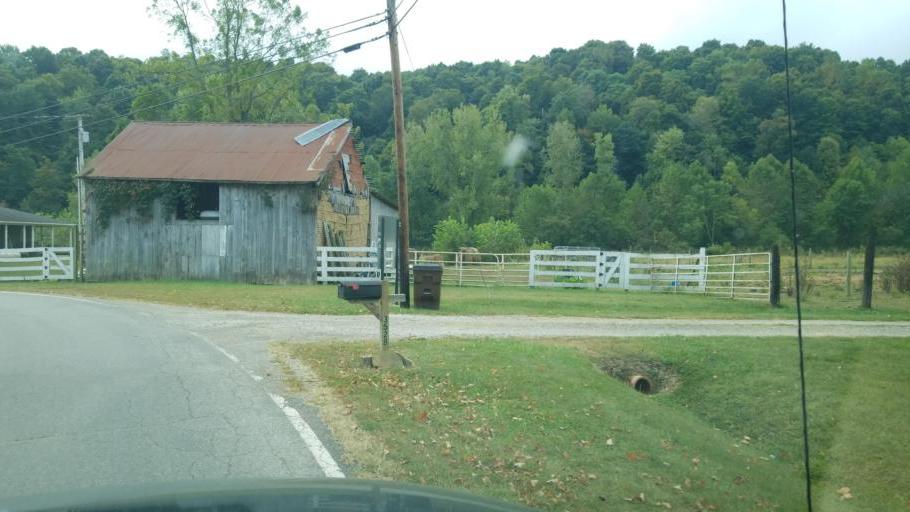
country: US
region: Ohio
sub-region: Licking County
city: Granville
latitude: 40.1210
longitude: -82.4753
